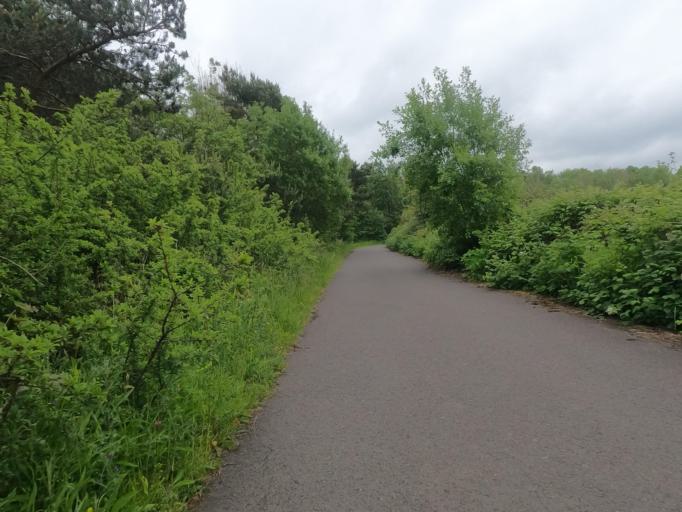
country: GB
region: England
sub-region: Northumberland
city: Bedlington
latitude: 55.1217
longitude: -1.5635
